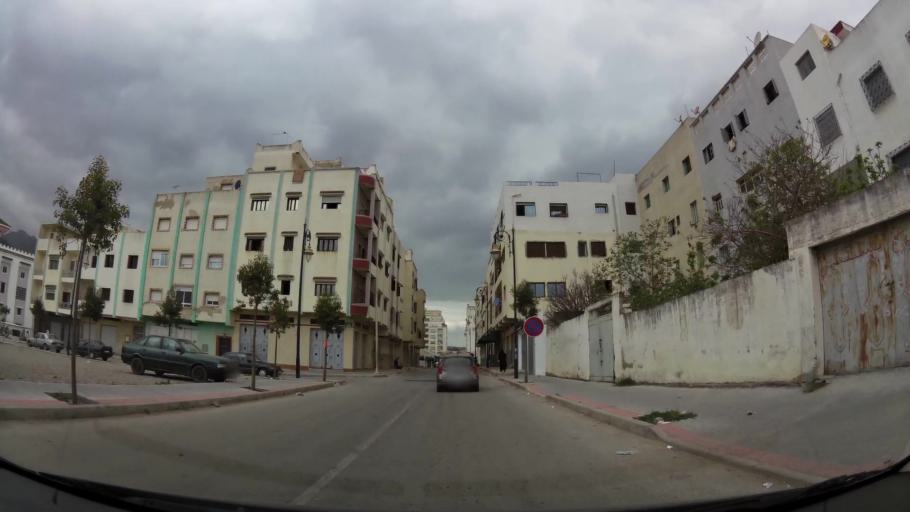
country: MA
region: Tanger-Tetouan
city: Tetouan
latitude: 35.5623
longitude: -5.3667
